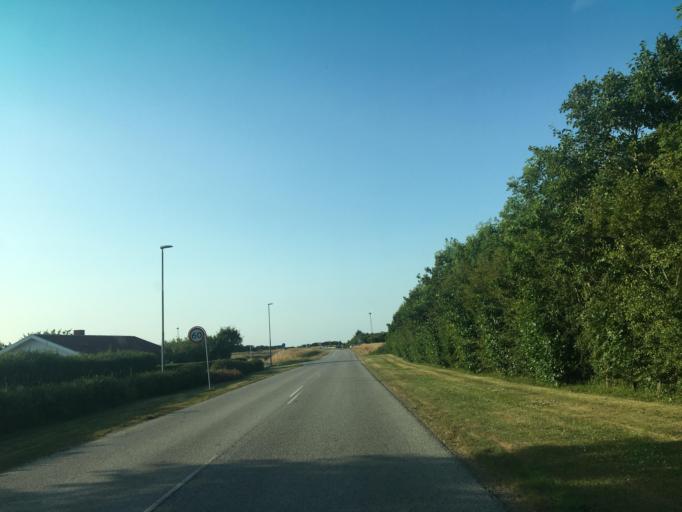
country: DK
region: North Denmark
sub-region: Thisted Kommune
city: Hurup
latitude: 56.7574
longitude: 8.4243
